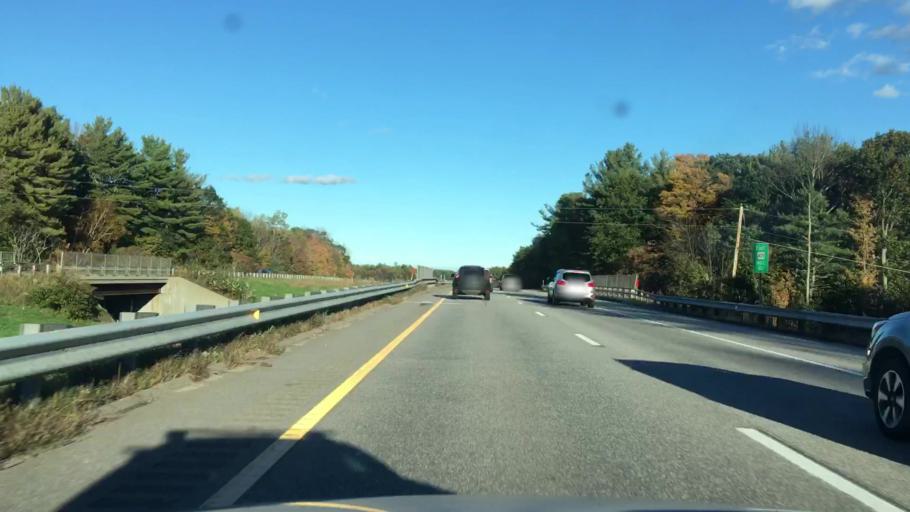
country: US
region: New Hampshire
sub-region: Rockingham County
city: Candia
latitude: 43.0398
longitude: -71.2939
